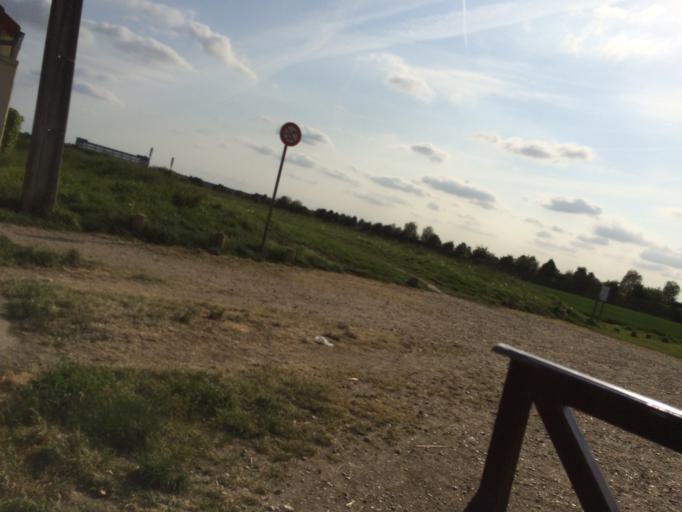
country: FR
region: Ile-de-France
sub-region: Departement de l'Essonne
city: Paray-Vieille-Poste
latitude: 48.7109
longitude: 2.3548
